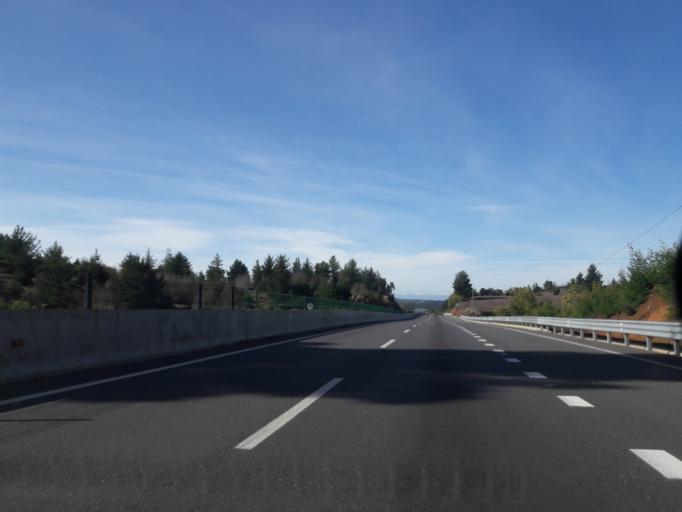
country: CL
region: Biobio
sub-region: Provincia de Biobio
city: Yumbel
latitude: -36.9634
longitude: -72.7092
